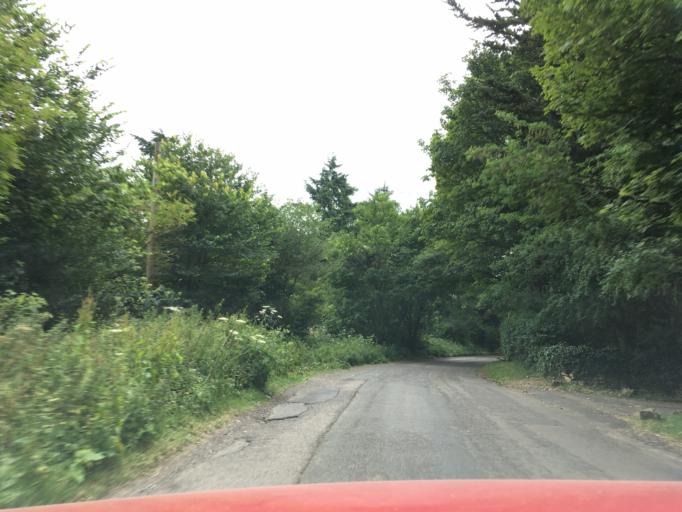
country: GB
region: England
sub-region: Oxfordshire
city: Chipping Norton
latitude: 51.9229
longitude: -1.5455
